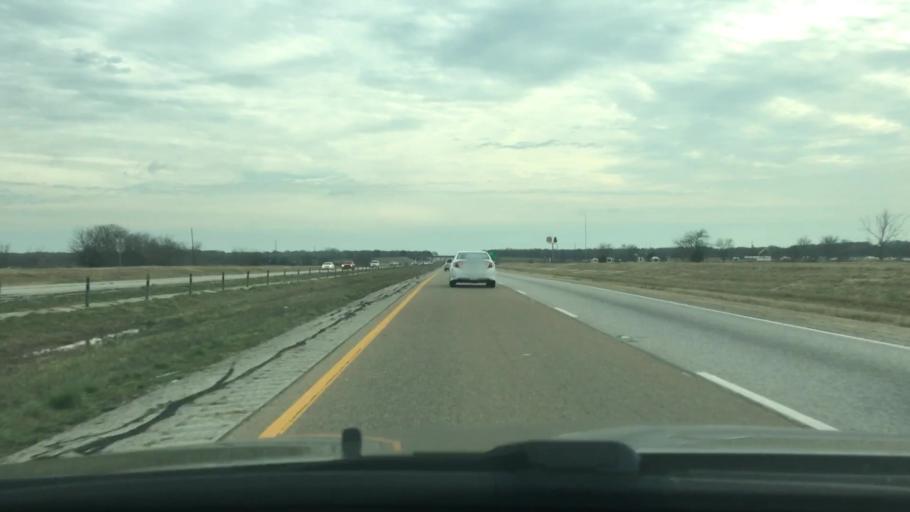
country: US
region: Texas
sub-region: Leon County
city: Centerville
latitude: 31.1006
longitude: -95.9639
